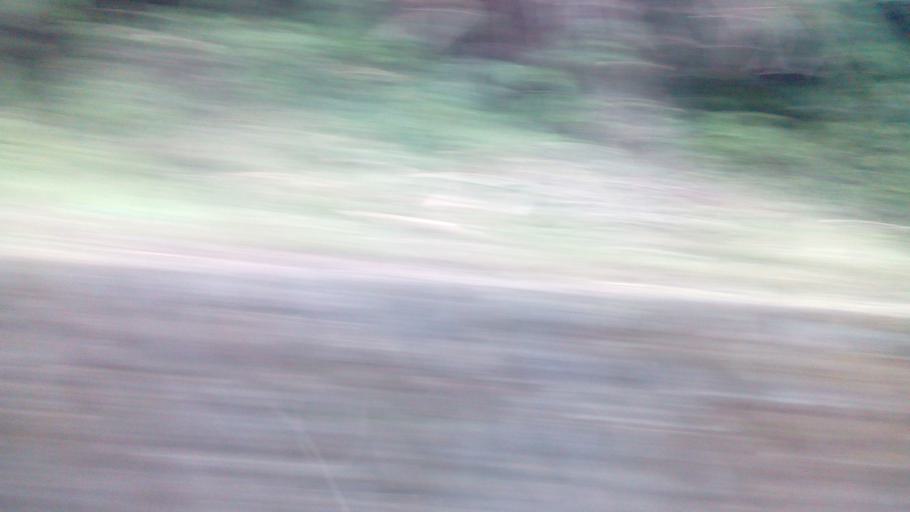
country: TW
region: Taiwan
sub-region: Yilan
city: Yilan
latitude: 24.5444
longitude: 121.4580
